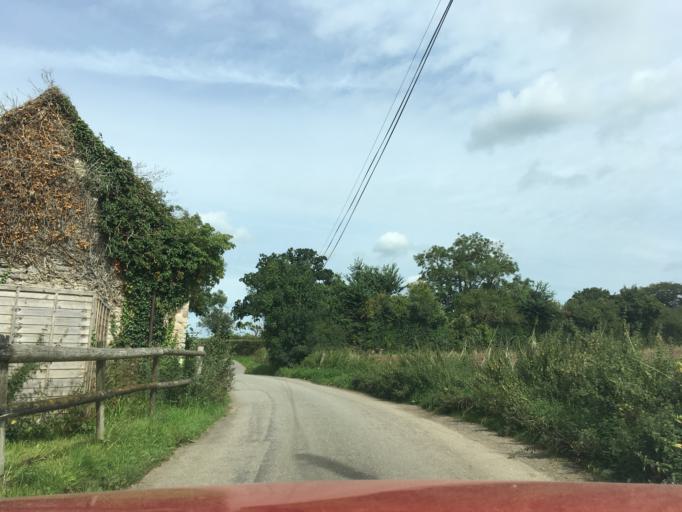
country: GB
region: England
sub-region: South Gloucestershire
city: Charfield
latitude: 51.6373
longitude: -2.4027
